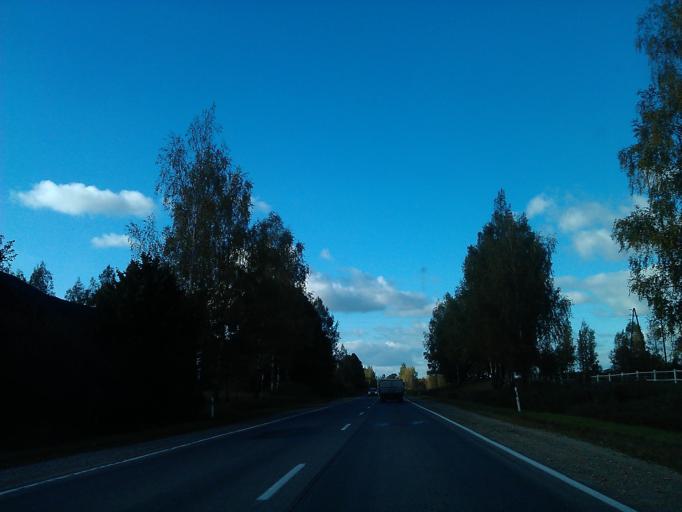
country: LV
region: Koknese
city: Koknese
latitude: 56.6346
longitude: 25.4548
